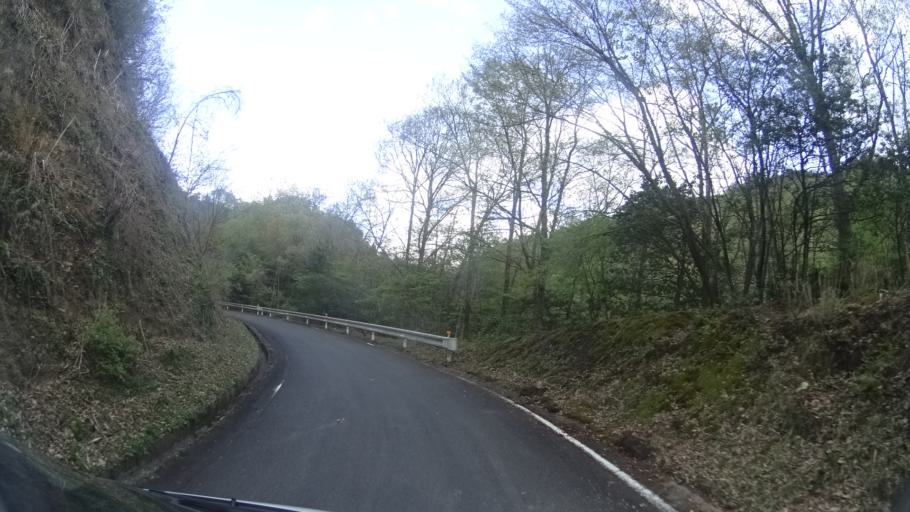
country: JP
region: Kyoto
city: Ayabe
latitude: 35.2576
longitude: 135.3187
